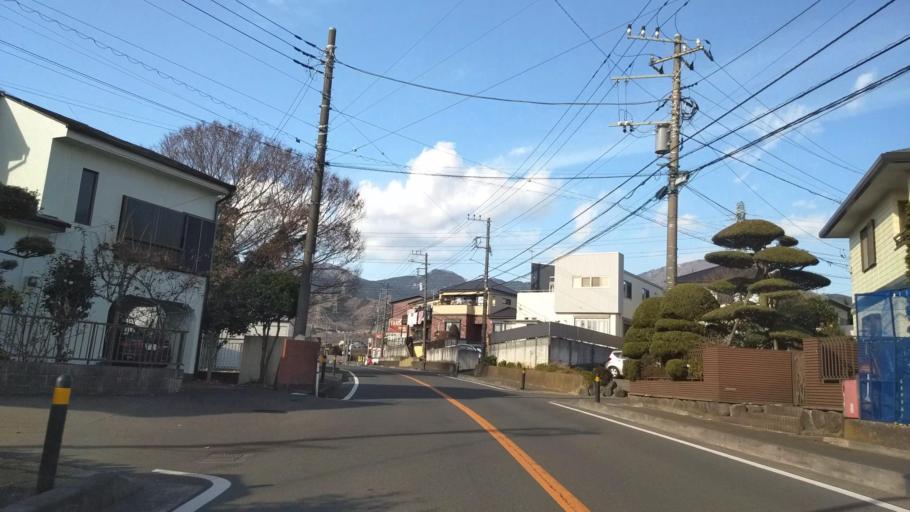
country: JP
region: Kanagawa
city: Hadano
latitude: 35.3860
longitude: 139.2370
